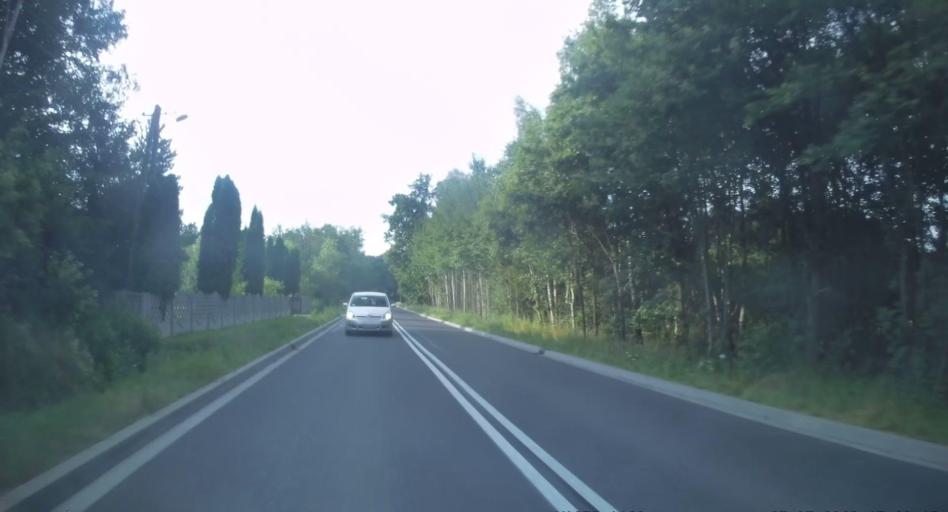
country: PL
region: Lesser Poland Voivodeship
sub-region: Powiat brzeski
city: Przyborow
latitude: 50.0427
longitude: 20.6462
